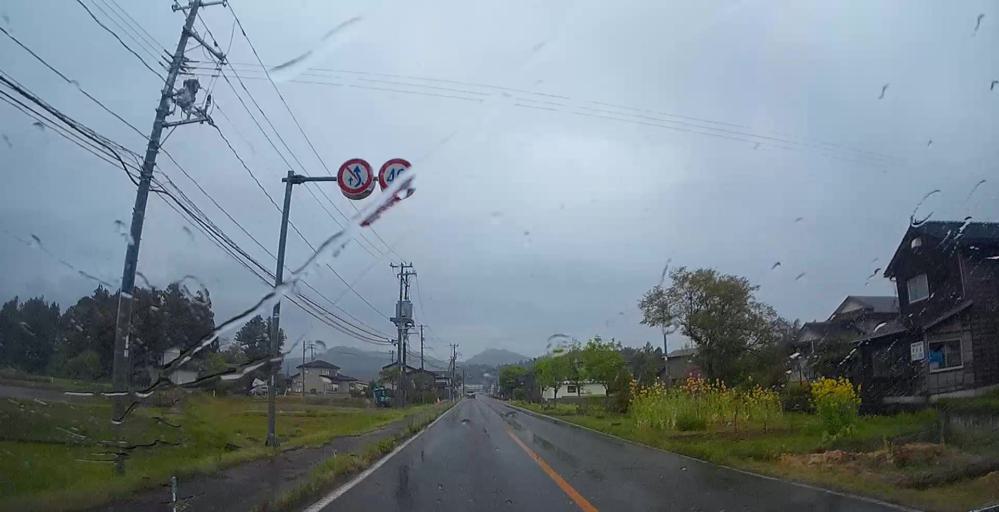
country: JP
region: Niigata
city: Kashiwazaki
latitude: 37.4462
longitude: 138.6467
